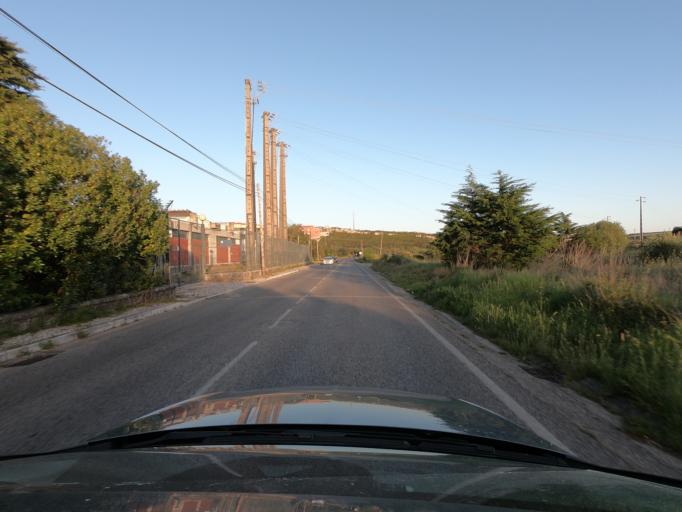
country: PT
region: Lisbon
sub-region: Sintra
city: Rio de Mouro
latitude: 38.7604
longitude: -9.3640
